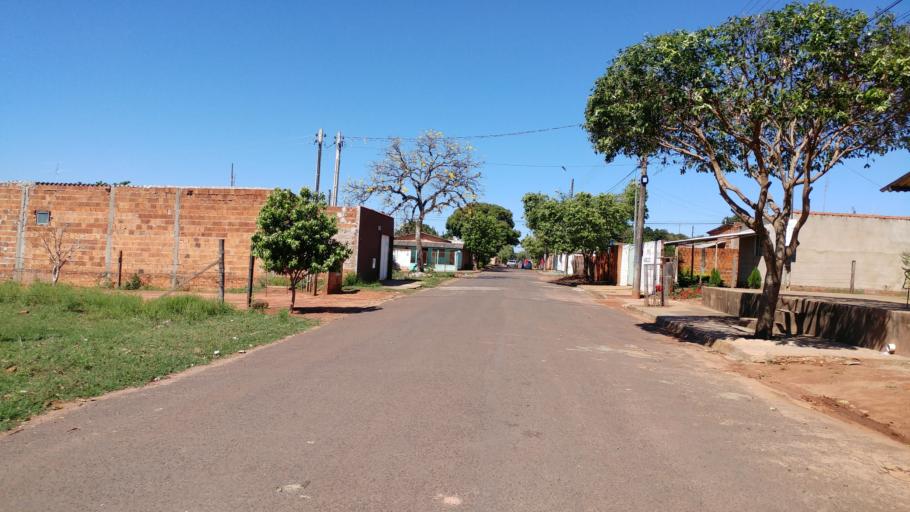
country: BR
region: Sao Paulo
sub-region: Paraguacu Paulista
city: Paraguacu Paulista
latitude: -22.4080
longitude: -50.5656
